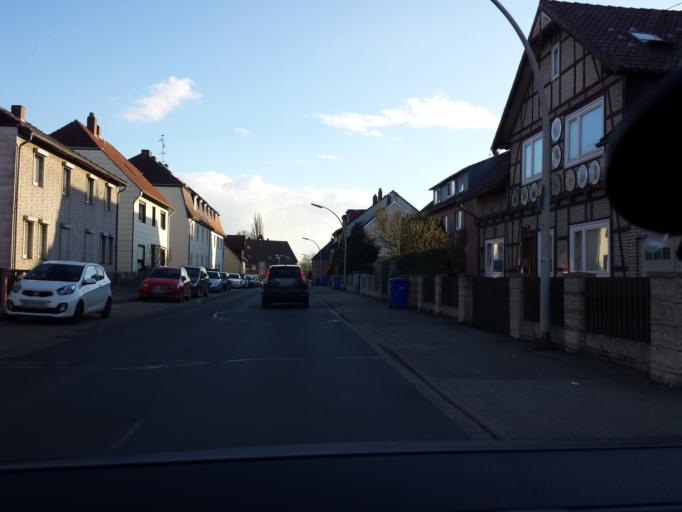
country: DE
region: Lower Saxony
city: Braunschweig
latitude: 52.3090
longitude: 10.4942
